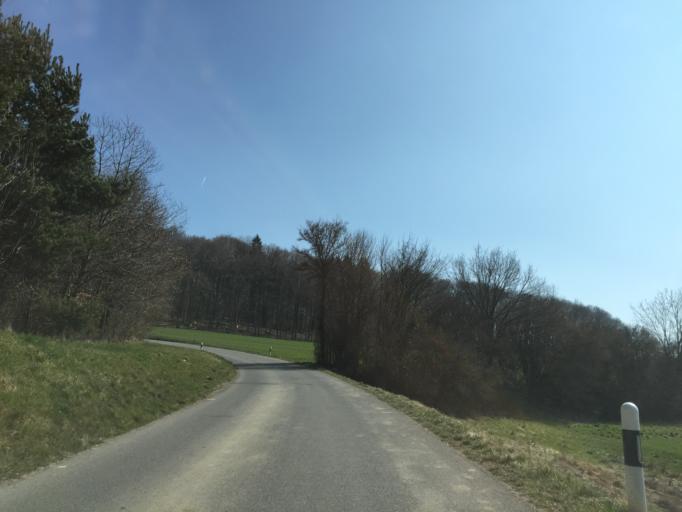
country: CH
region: Vaud
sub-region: Morges District
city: Chevilly
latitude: 46.6387
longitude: 6.4835
